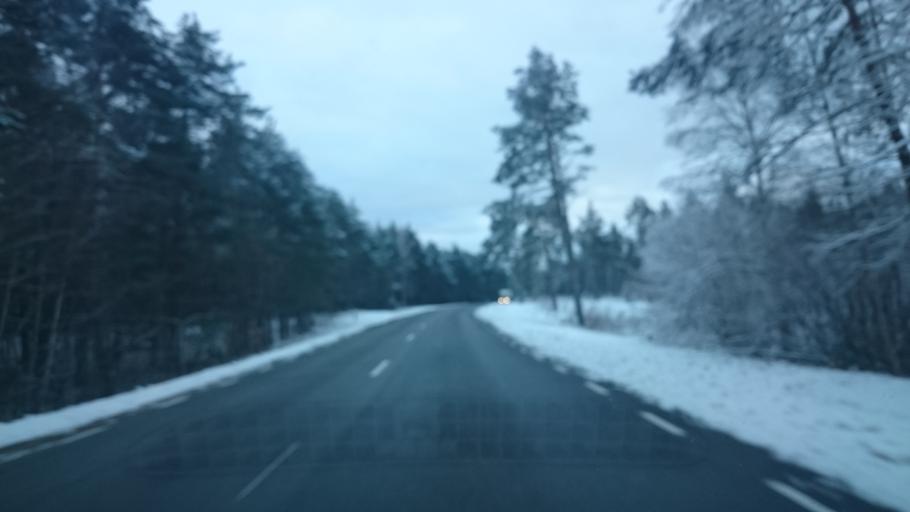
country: EE
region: Saare
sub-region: Kuressaare linn
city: Kuressaare
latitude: 58.3950
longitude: 22.6464
